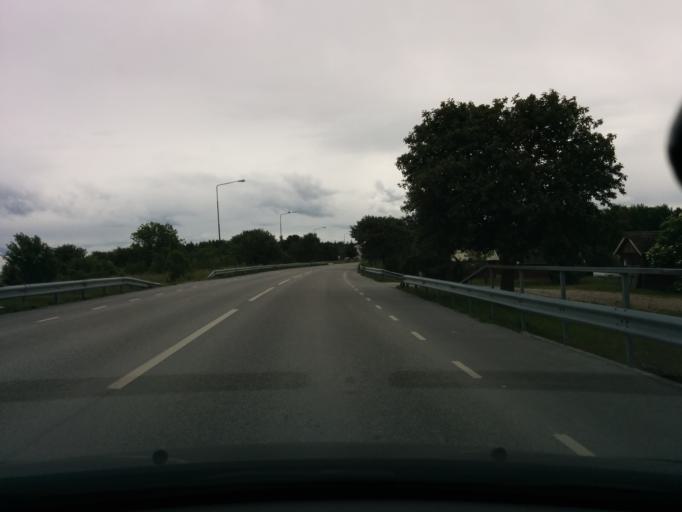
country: SE
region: Gotland
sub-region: Gotland
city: Slite
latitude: 57.6951
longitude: 18.7987
